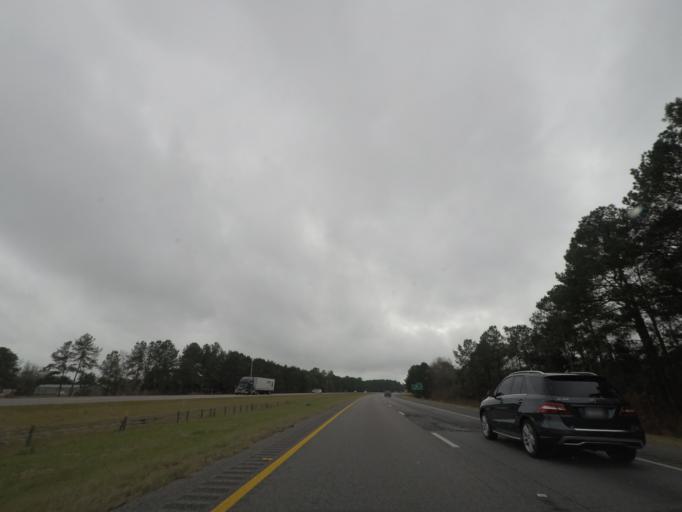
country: US
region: South Carolina
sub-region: Orangeburg County
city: Holly Hill
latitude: 33.4189
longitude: -80.4939
